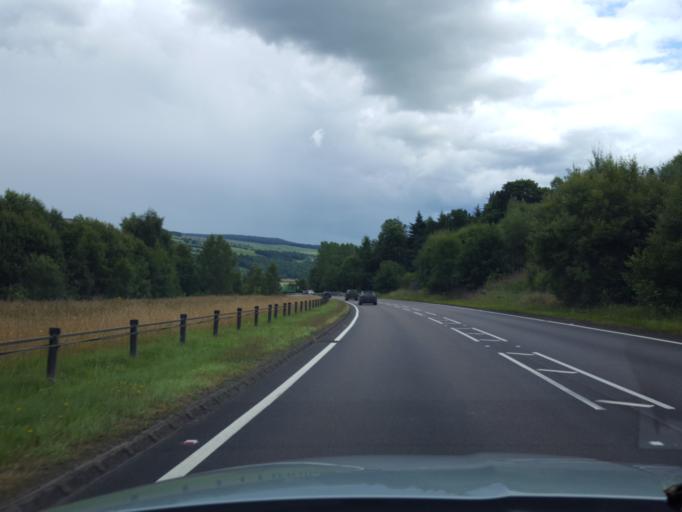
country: GB
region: Scotland
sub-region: Perth and Kinross
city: Pitlochry
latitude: 56.6923
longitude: -3.7261
